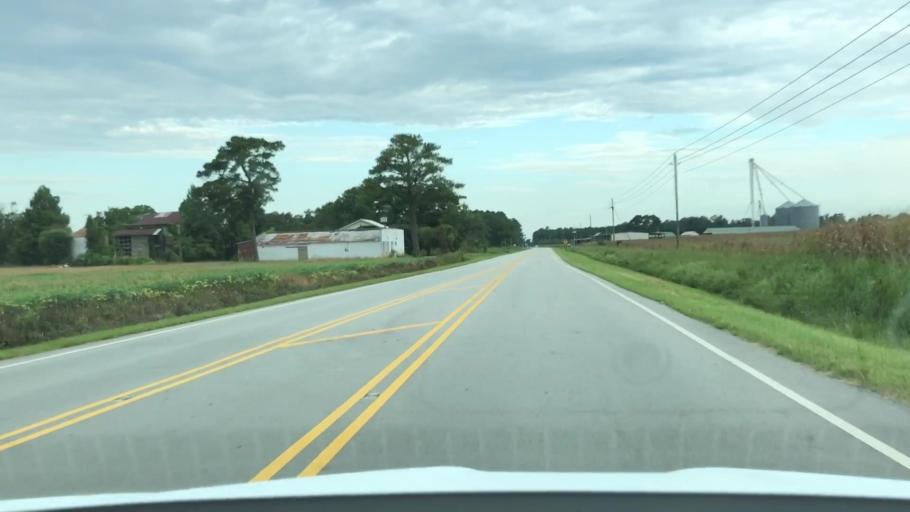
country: US
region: North Carolina
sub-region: Jones County
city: Trenton
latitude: 35.0685
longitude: -77.3680
